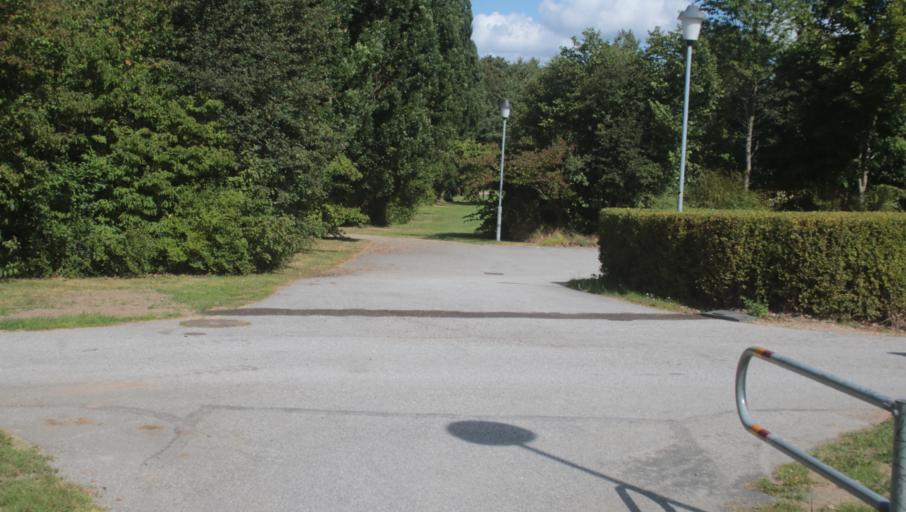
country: SE
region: Blekinge
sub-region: Karlshamns Kommun
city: Karlshamn
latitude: 56.2054
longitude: 14.8269
